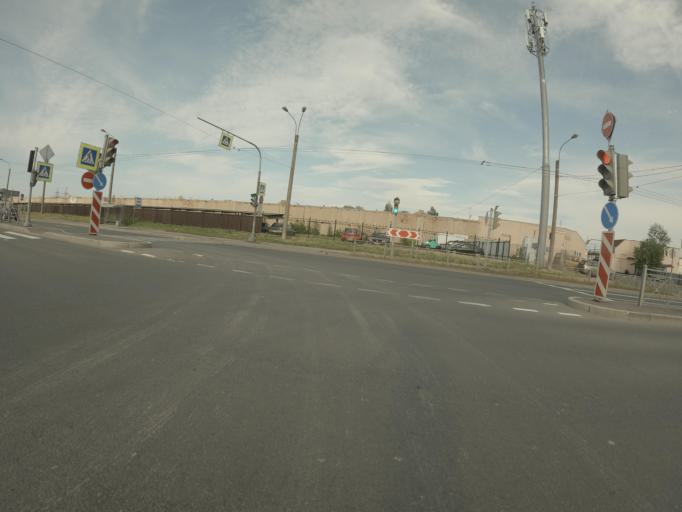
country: RU
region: St.-Petersburg
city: Krasnogvargeisky
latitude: 59.9393
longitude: 30.5040
